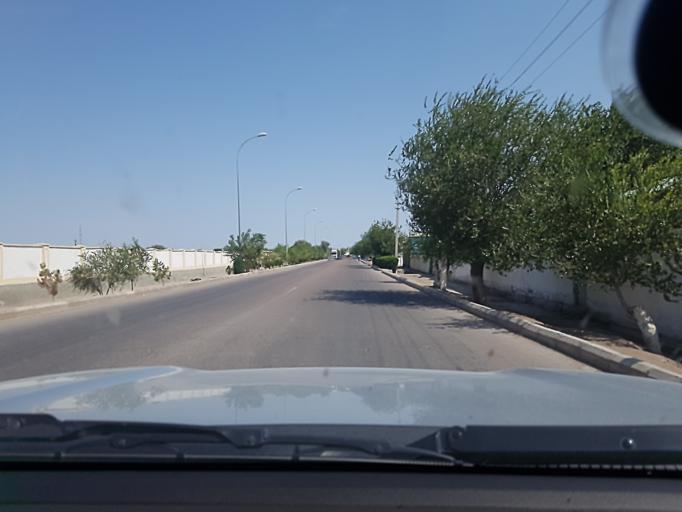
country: TM
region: Dasoguz
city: Koeneuergench
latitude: 42.3244
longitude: 59.1427
